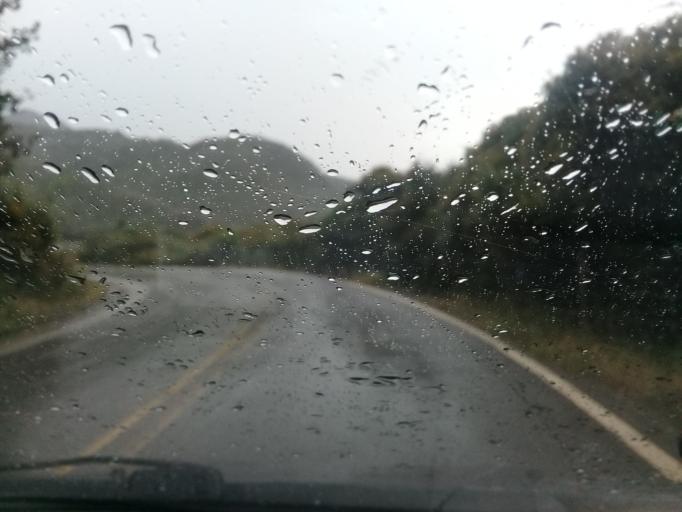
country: CO
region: Cundinamarca
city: Guasca
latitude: 4.8456
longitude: -73.8254
